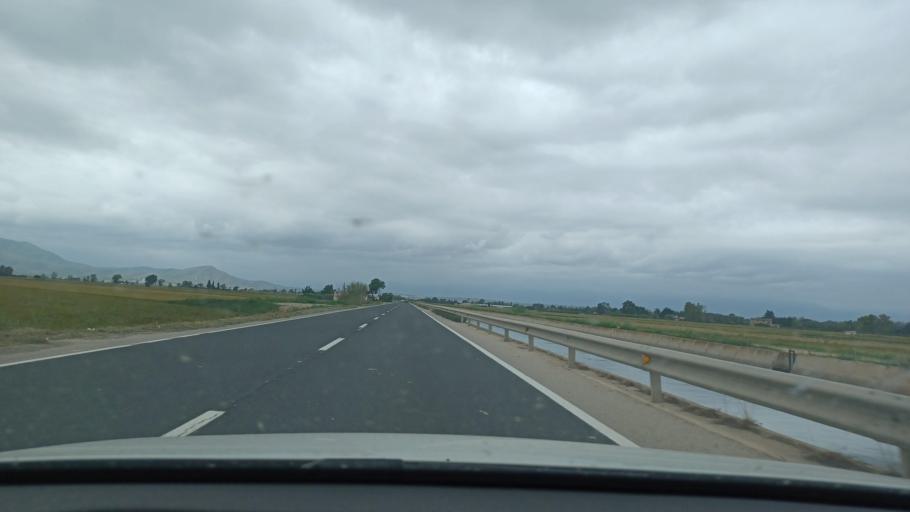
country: ES
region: Catalonia
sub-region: Provincia de Tarragona
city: Deltebre
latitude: 40.7101
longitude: 0.6536
